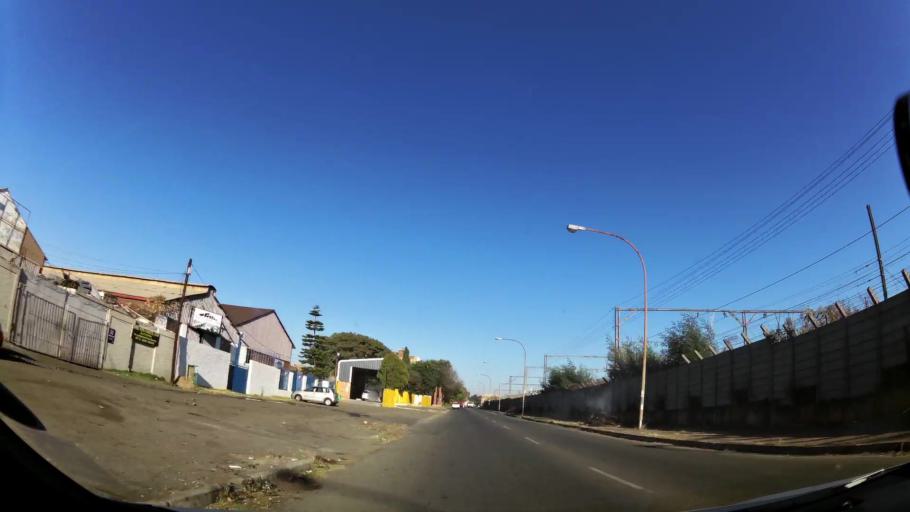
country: ZA
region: Gauteng
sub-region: City of Johannesburg Metropolitan Municipality
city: Johannesburg
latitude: -26.2071
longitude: 28.0828
